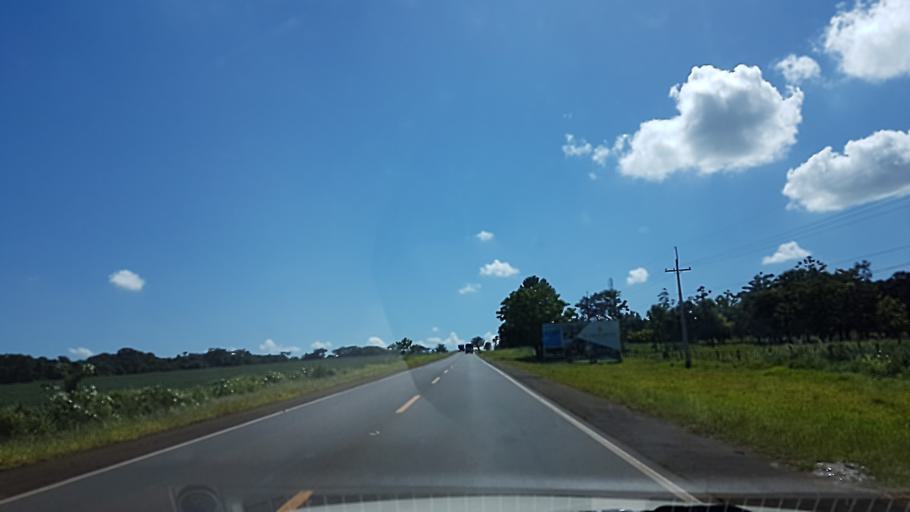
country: PY
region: Itapua
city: San Juan del Parana
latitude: -27.2074
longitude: -56.0740
